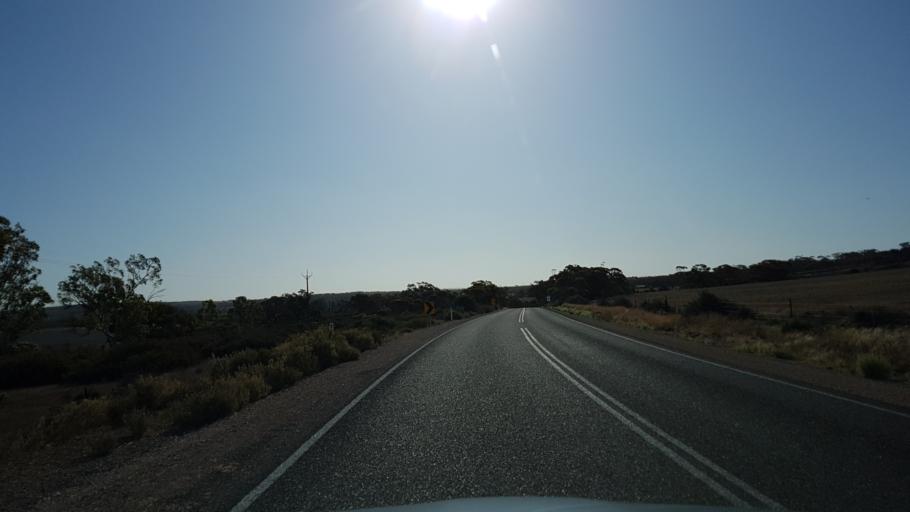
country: AU
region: South Australia
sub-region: Mid Murray
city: Mannum
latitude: -34.8554
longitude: 139.4123
